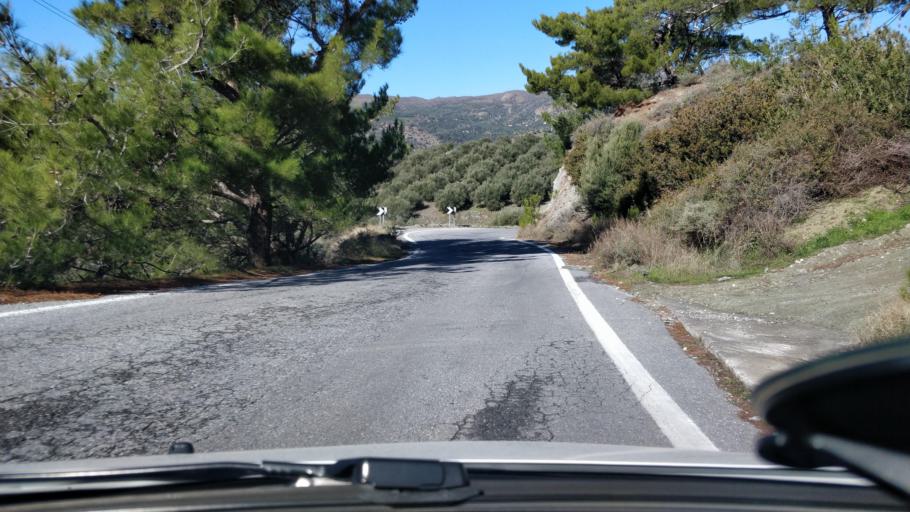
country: GR
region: Crete
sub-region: Nomos Irakleiou
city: Arkalochori
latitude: 35.0055
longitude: 25.4385
